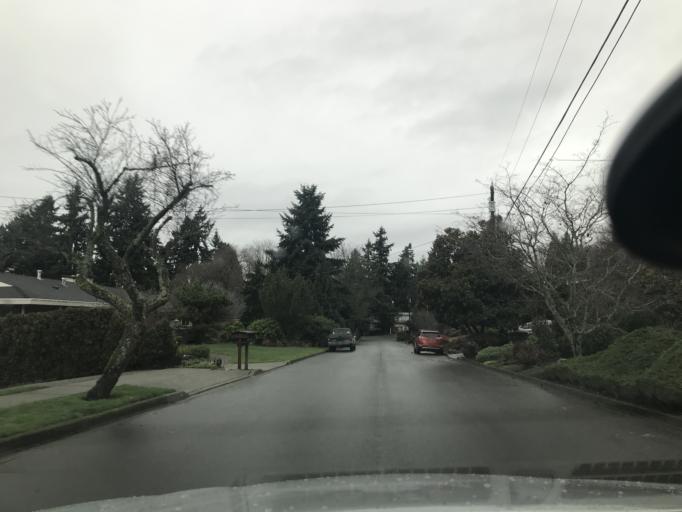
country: US
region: Washington
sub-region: King County
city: Kirkland
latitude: 47.6648
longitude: -122.1896
